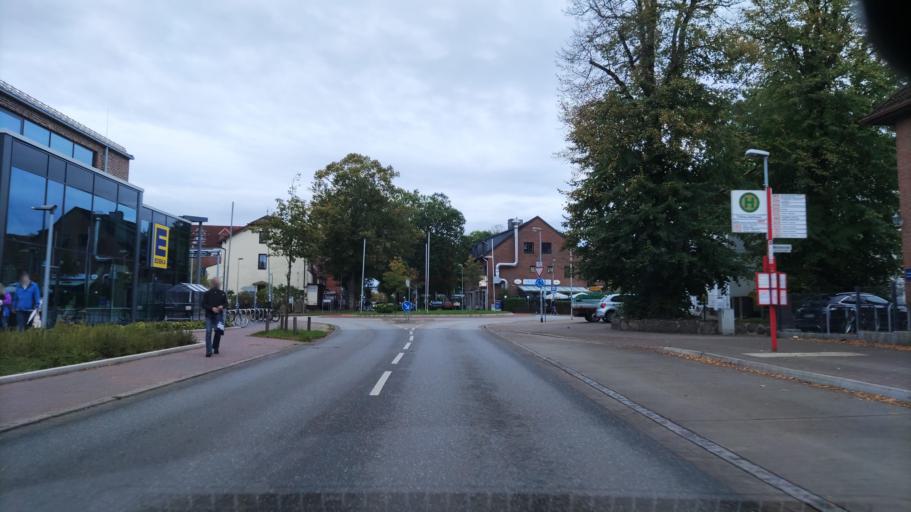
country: DE
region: Schleswig-Holstein
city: Trittau
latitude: 53.6100
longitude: 10.4066
